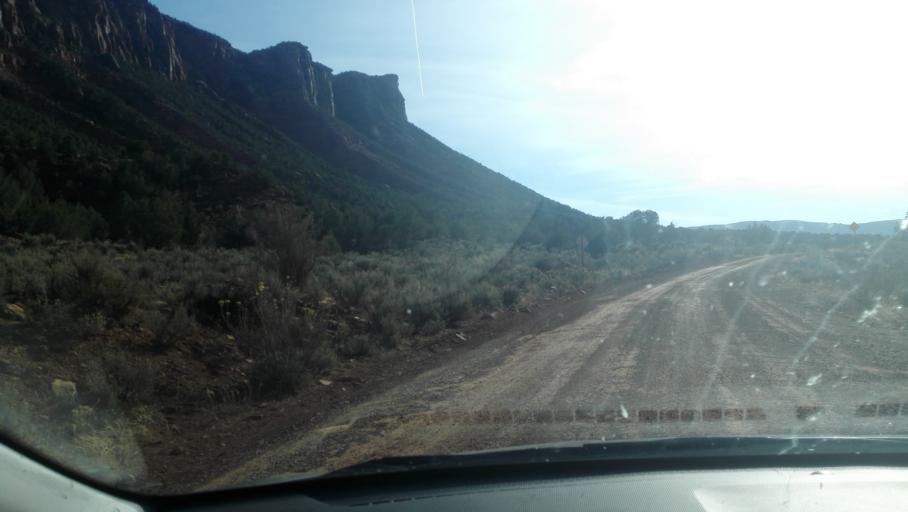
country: US
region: Colorado
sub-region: Dolores County
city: Dove Creek
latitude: 38.3579
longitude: -108.8298
